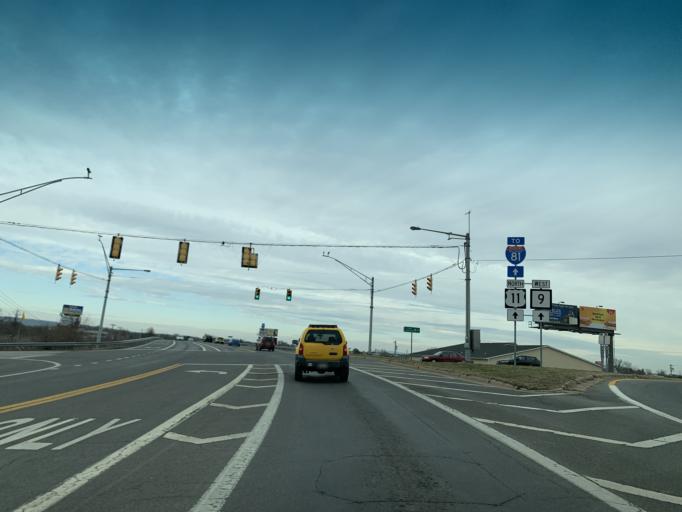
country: US
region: West Virginia
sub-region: Berkeley County
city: Martinsburg
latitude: 39.4722
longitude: -77.9551
